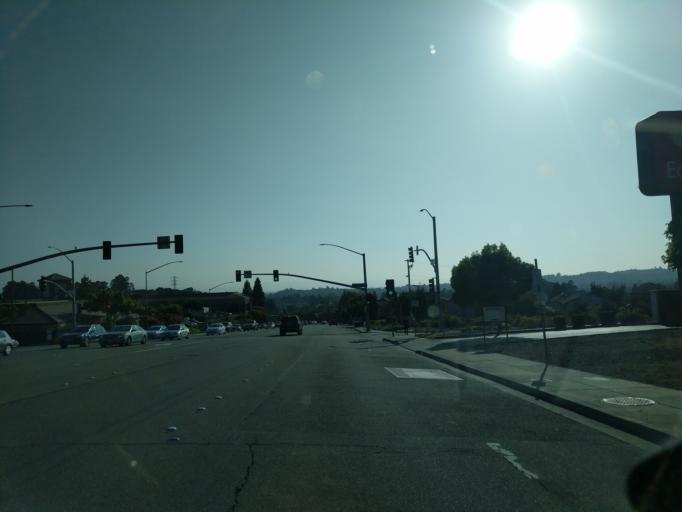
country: US
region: California
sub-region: Alameda County
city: Fairview
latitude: 37.6958
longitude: -122.0511
